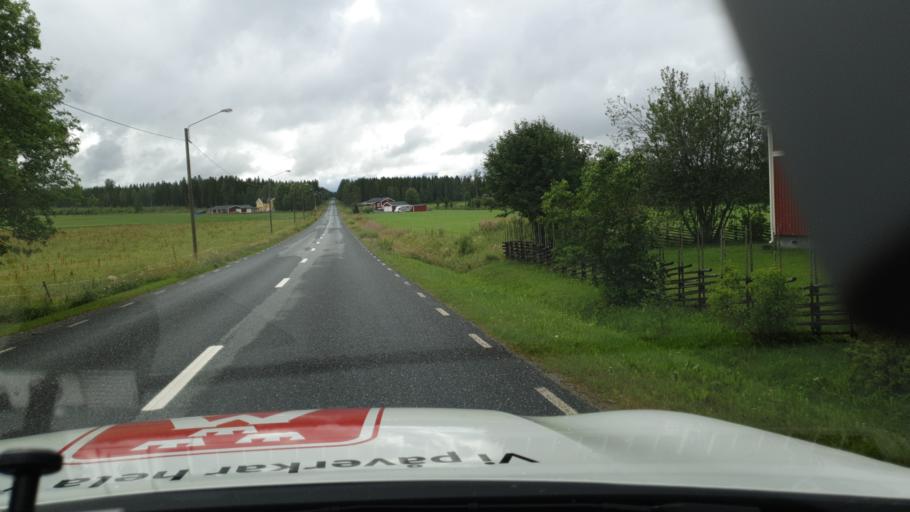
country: SE
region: Vaesterbotten
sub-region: Skelleftea Kommun
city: Storvik
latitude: 64.9740
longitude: 20.6953
